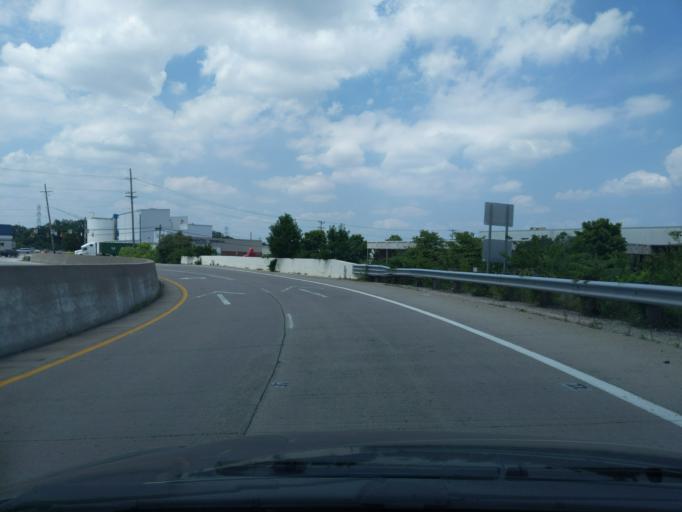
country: US
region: Ohio
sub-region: Hamilton County
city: Sharonville
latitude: 39.2882
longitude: -84.4274
